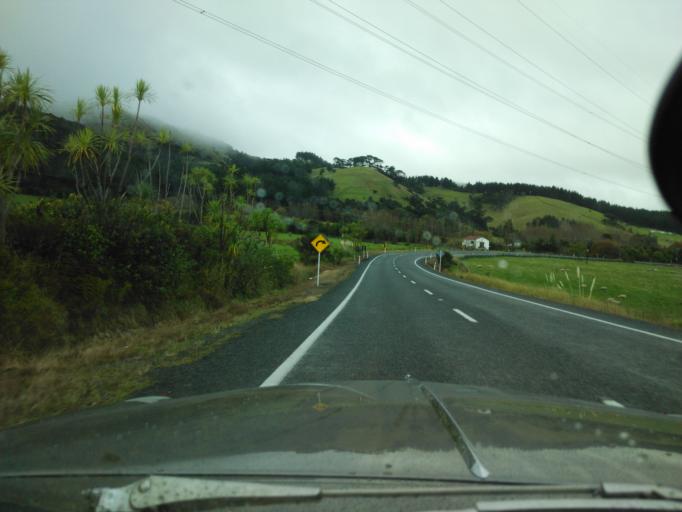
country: NZ
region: Auckland
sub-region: Auckland
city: Parakai
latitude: -36.4809
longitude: 174.4487
